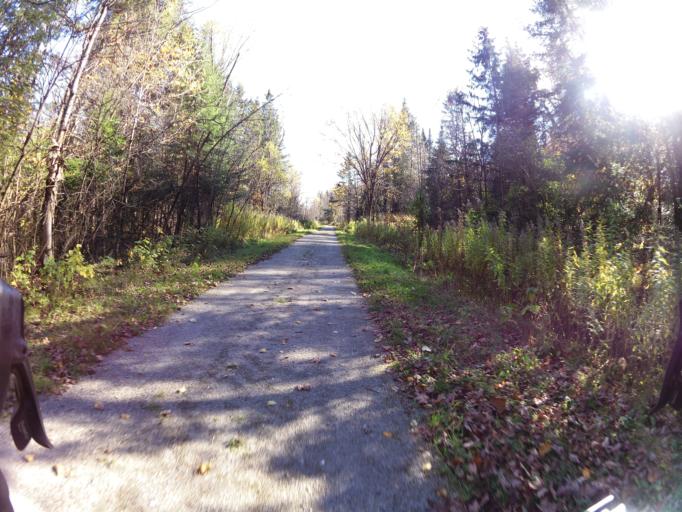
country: CA
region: Quebec
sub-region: Outaouais
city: Wakefield
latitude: 45.8163
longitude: -75.9628
